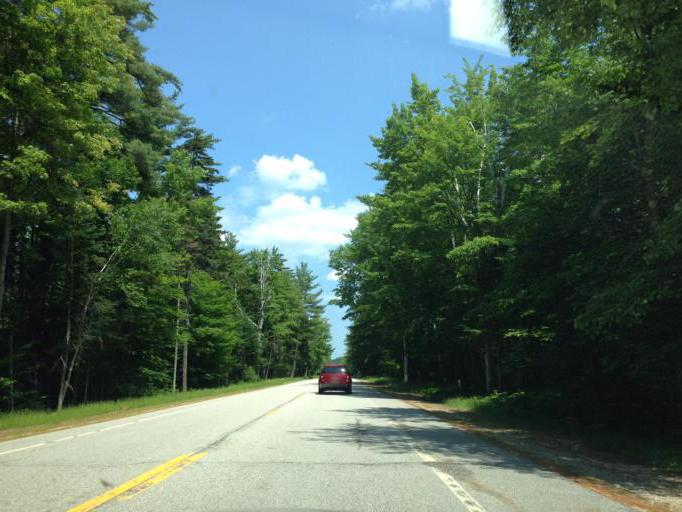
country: US
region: New Hampshire
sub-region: Carroll County
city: Tamworth
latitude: 43.9894
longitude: -71.3052
